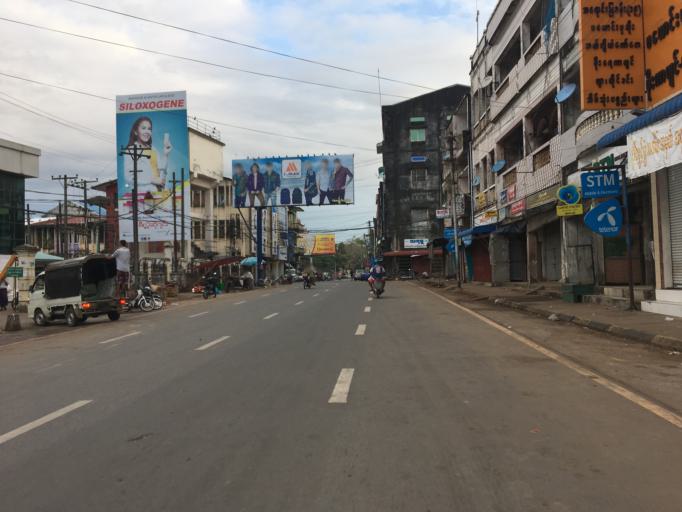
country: MM
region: Mon
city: Mawlamyine
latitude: 16.4944
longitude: 97.6191
